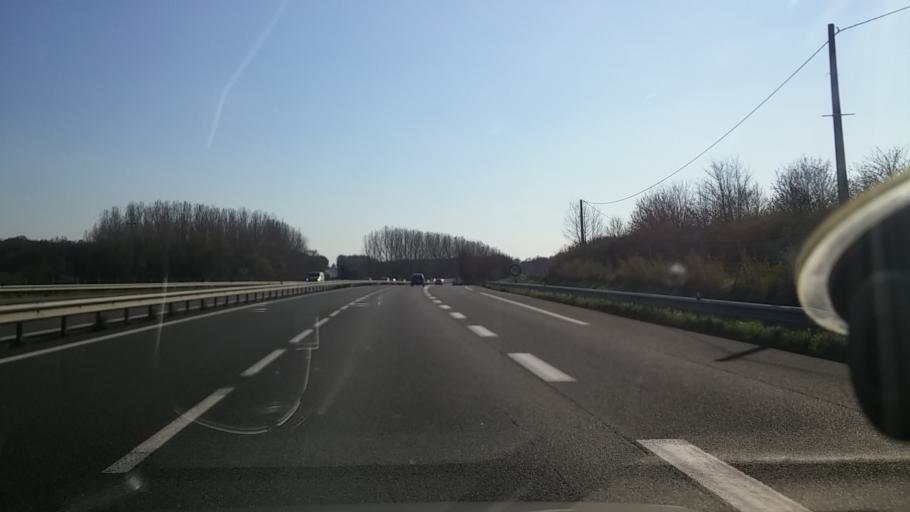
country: FR
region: Centre
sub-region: Departement du Cher
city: Massay
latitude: 47.1765
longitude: 2.0094
